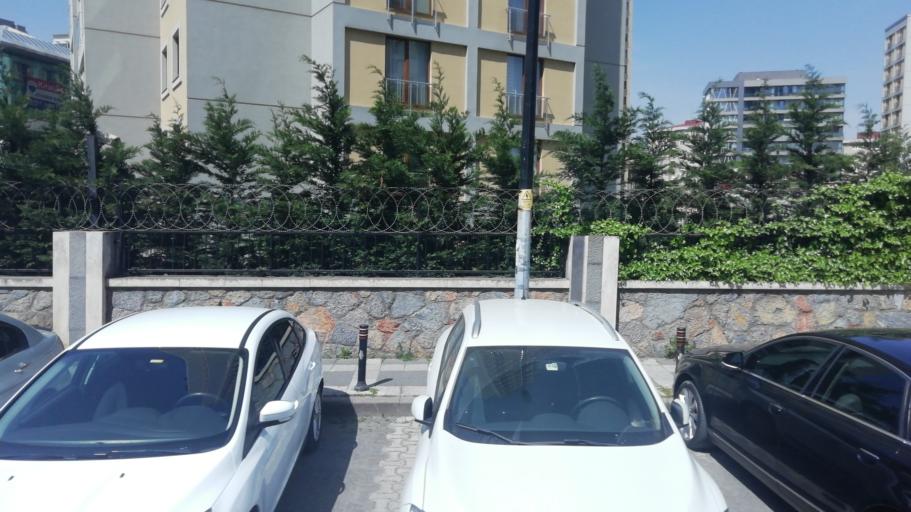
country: TR
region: Istanbul
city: Umraniye
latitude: 40.9985
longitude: 29.1399
